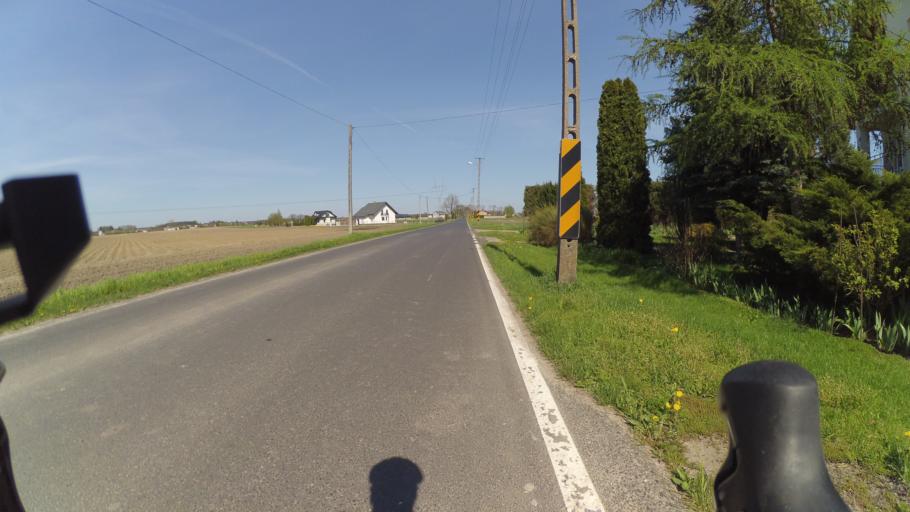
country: PL
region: Masovian Voivodeship
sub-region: Powiat warszawski zachodni
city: Leszno
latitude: 52.2488
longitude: 20.5574
